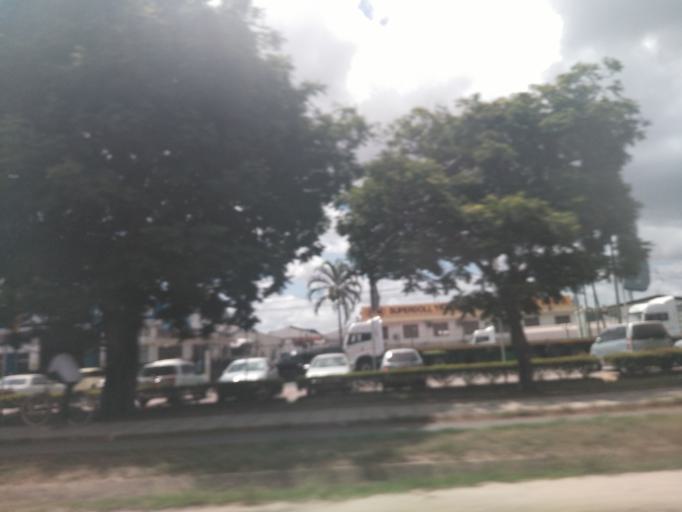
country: TZ
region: Dar es Salaam
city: Dar es Salaam
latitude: -6.8383
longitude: 39.2574
